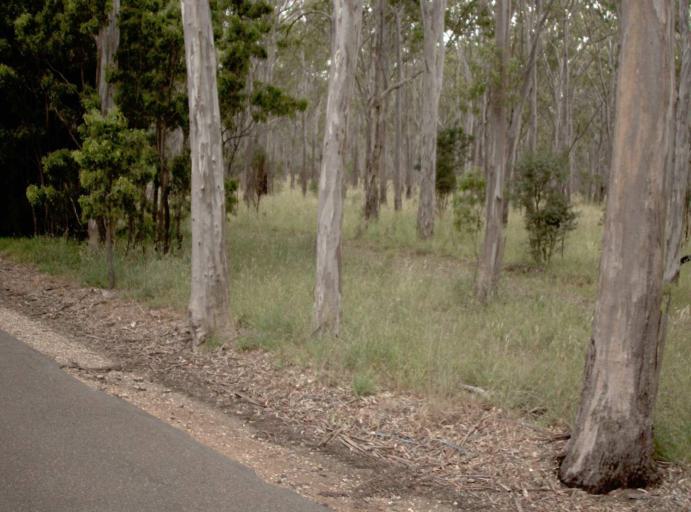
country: AU
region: Victoria
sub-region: Wellington
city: Sale
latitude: -37.8609
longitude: 147.0692
